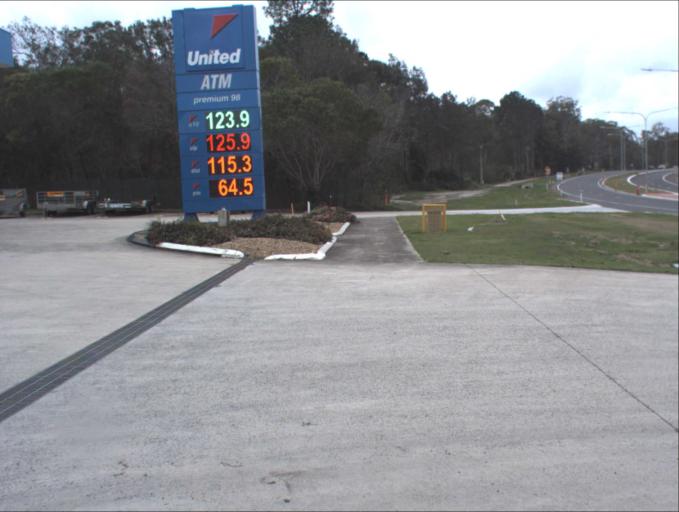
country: AU
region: Queensland
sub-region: Logan
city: Logan Reserve
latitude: -27.7082
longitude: 153.0935
